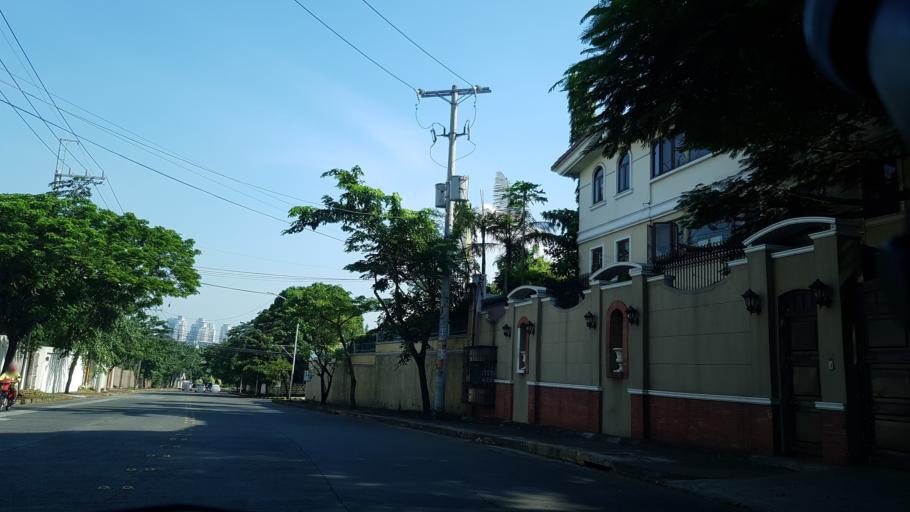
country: PH
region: Metro Manila
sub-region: Pasig
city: Pasig City
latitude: 14.5990
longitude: 121.0712
